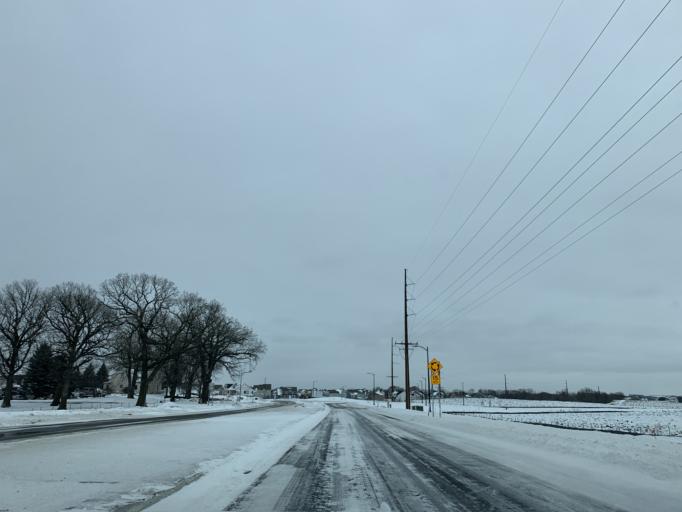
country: US
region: Minnesota
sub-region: Carver County
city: Chaska
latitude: 44.7910
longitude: -93.6276
